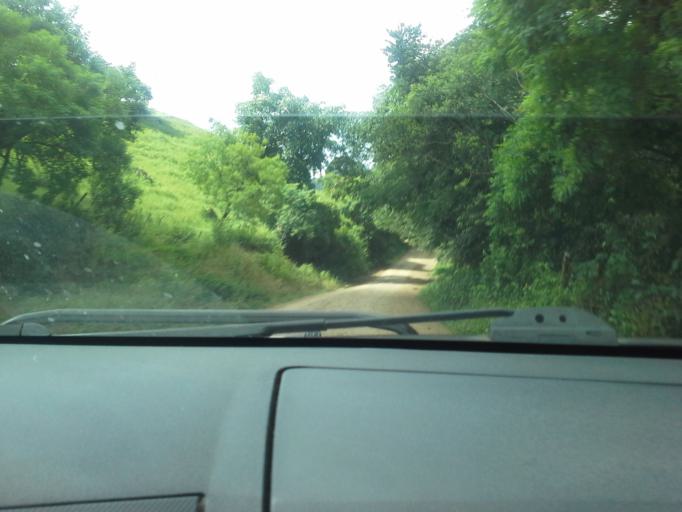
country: NI
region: Matagalpa
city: Terrabona
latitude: 12.7242
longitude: -85.9651
